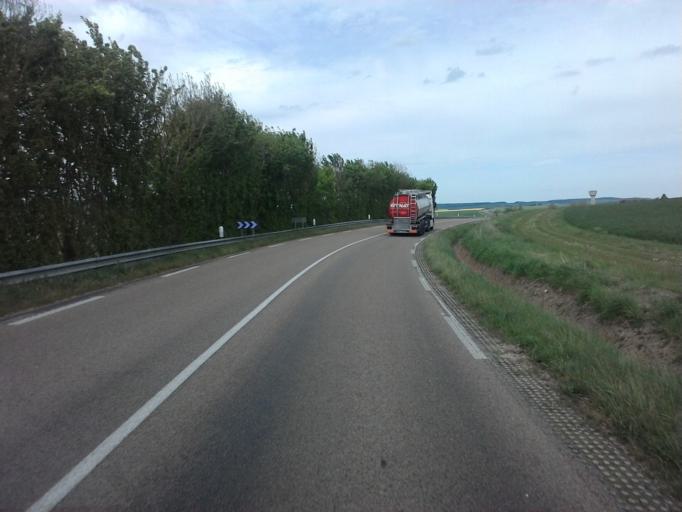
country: FR
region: Bourgogne
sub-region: Departement de l'Yonne
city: Neuvy-Sautour
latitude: 48.0608
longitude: 3.8039
